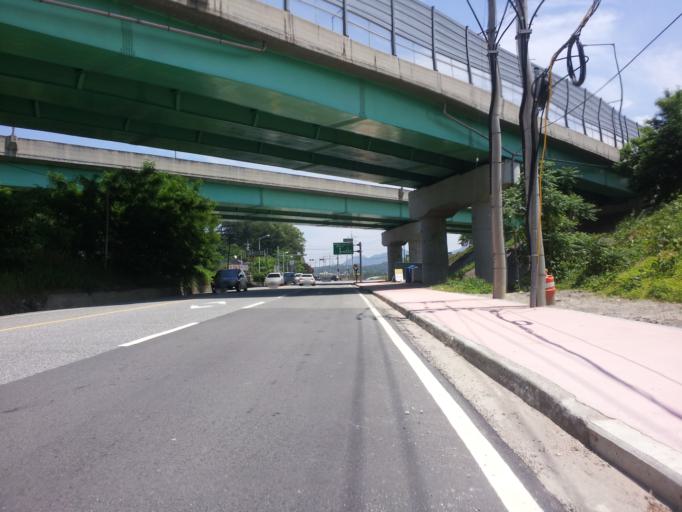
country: KR
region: Chungcheongbuk-do
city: Okcheon
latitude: 36.3116
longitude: 127.5675
